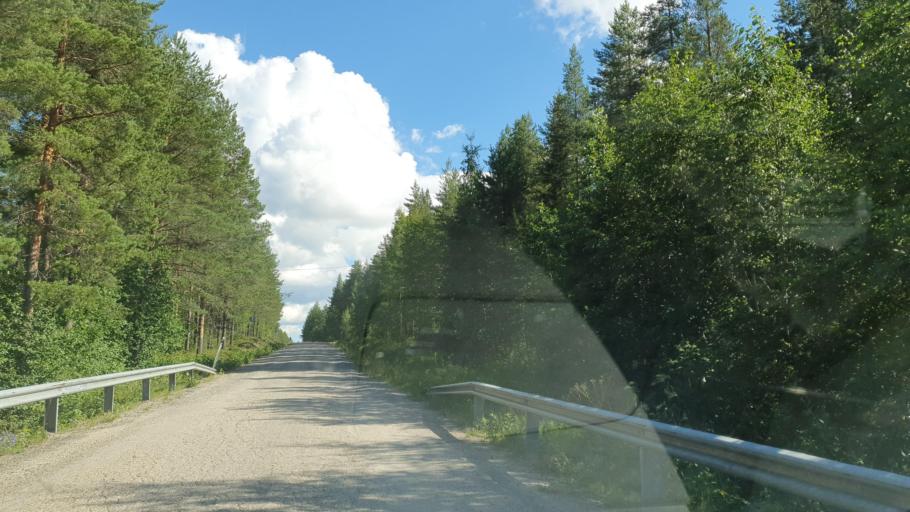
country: FI
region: Kainuu
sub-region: Kehys-Kainuu
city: Kuhmo
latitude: 64.1085
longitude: 29.3864
